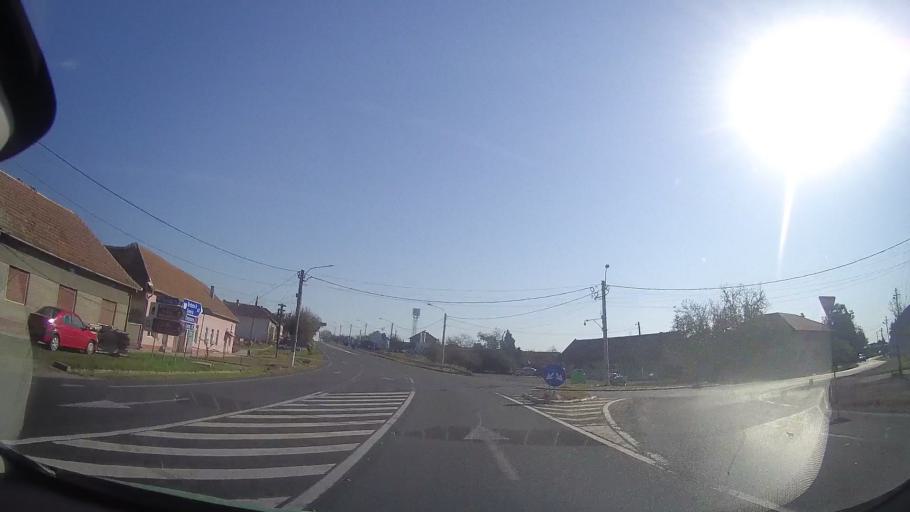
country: RO
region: Timis
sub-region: Comuna Topolovatu Mare
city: Topolovatu Mare
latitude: 45.7738
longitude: 21.6238
